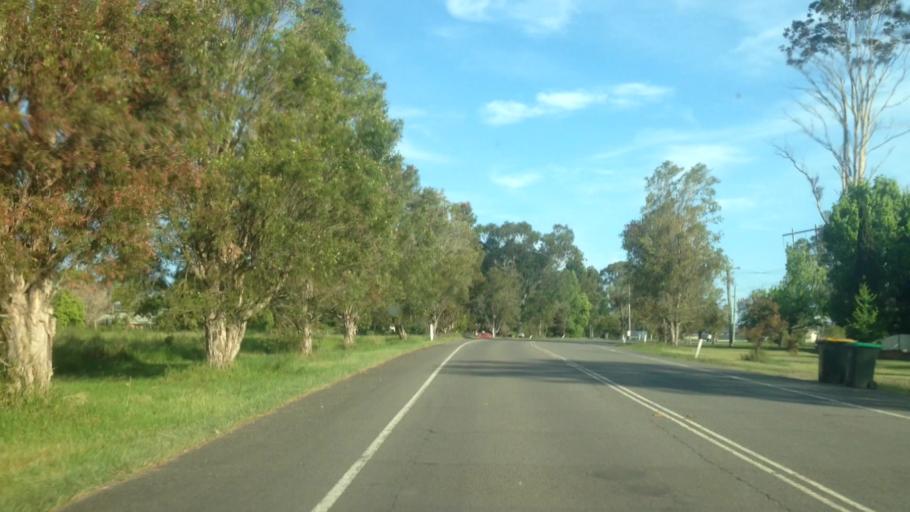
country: AU
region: New South Wales
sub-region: Lake Macquarie Shire
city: Dora Creek
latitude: -33.1021
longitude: 151.4764
